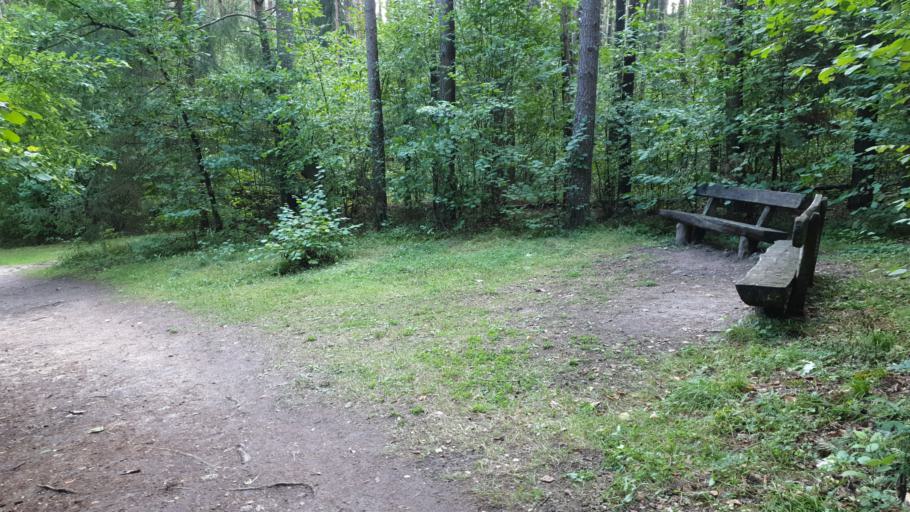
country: LT
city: Trakai
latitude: 54.6454
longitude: 24.9669
